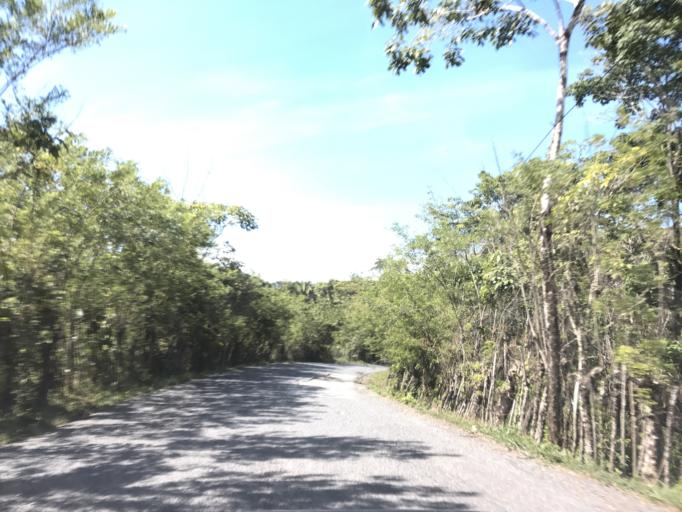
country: GT
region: Izabal
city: Morales
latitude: 15.6415
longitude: -89.0307
